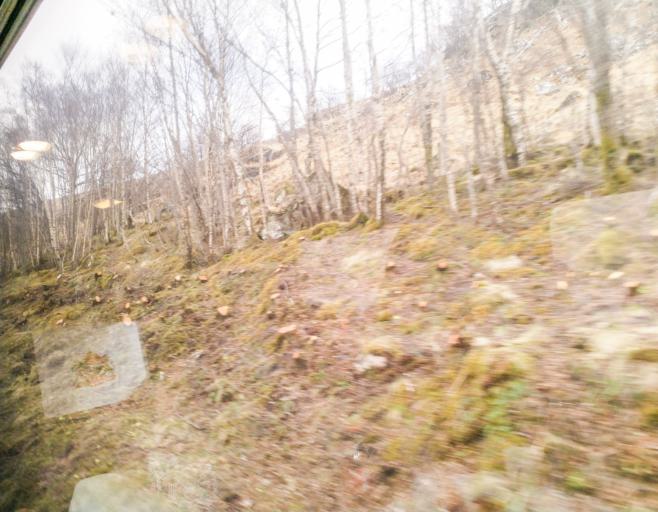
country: GB
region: Scotland
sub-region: Highland
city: Spean Bridge
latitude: 56.7956
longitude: -4.7238
